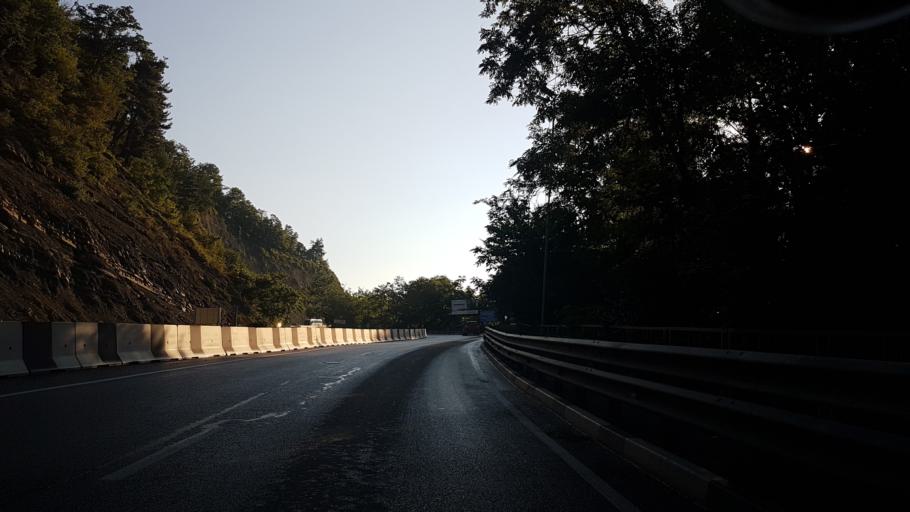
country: RU
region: Krasnodarskiy
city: Dagomys
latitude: 43.6403
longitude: 39.6980
